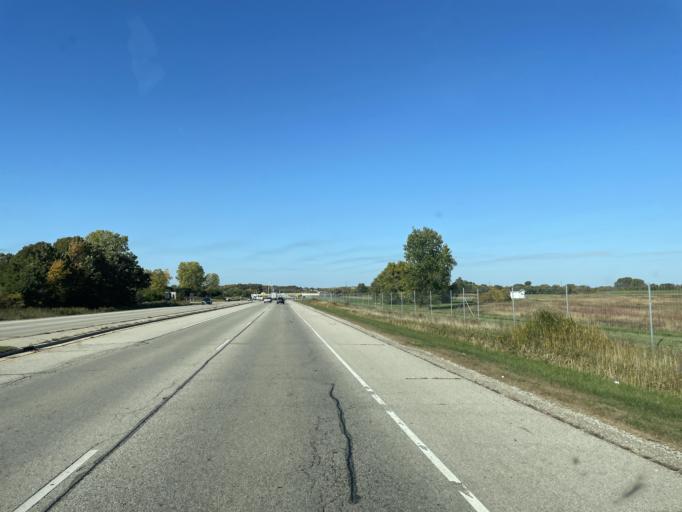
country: US
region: Wisconsin
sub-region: Kenosha County
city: Pleasant Prairie
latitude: 42.5897
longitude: -87.9430
